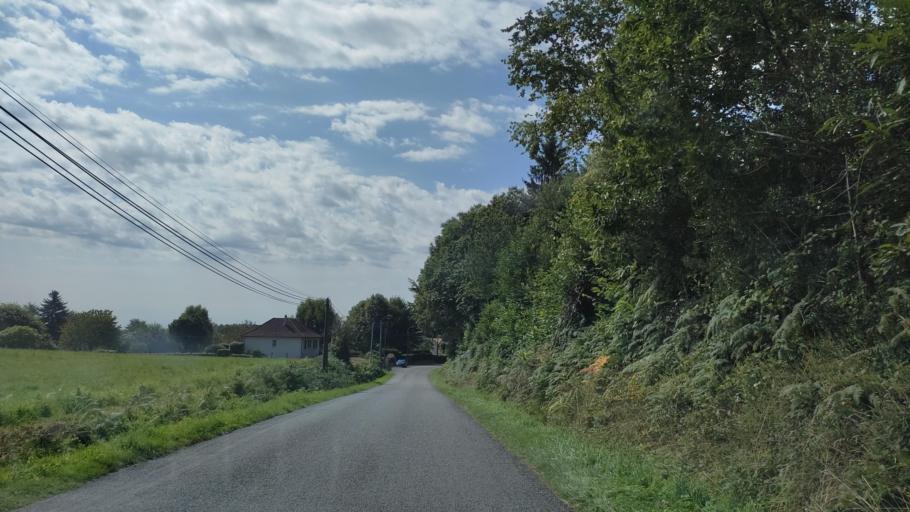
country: FR
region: Limousin
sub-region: Departement de la Haute-Vienne
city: Couzeix
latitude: 45.8497
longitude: 1.1925
